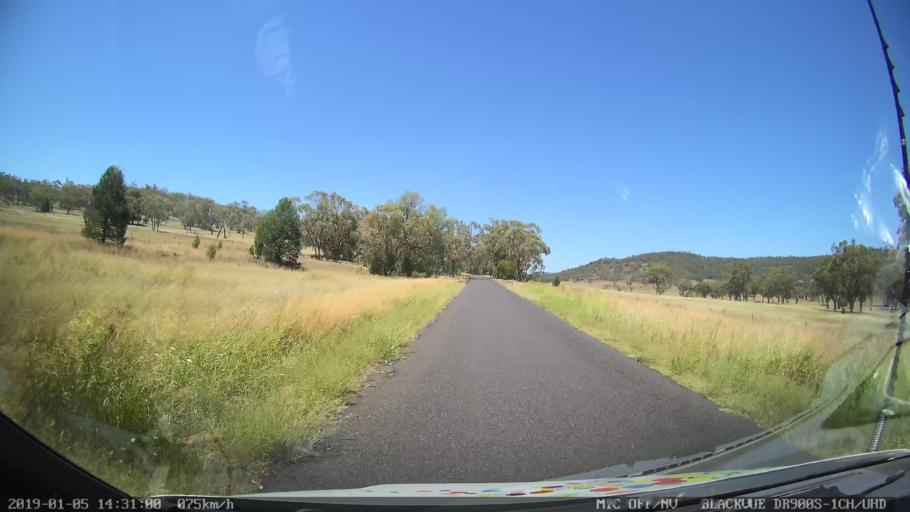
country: AU
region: New South Wales
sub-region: Tamworth Municipality
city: Phillip
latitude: -31.2268
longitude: 150.6002
